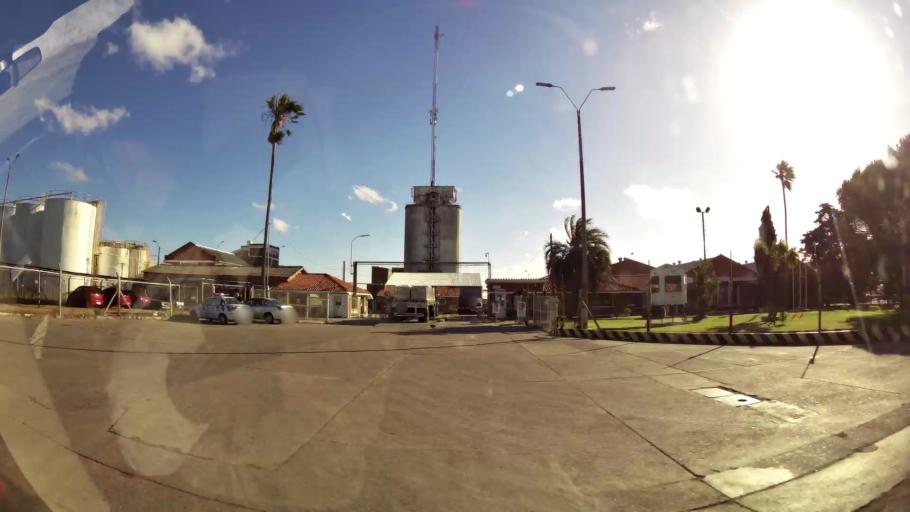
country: UY
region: Montevideo
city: Montevideo
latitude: -34.8481
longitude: -56.2466
